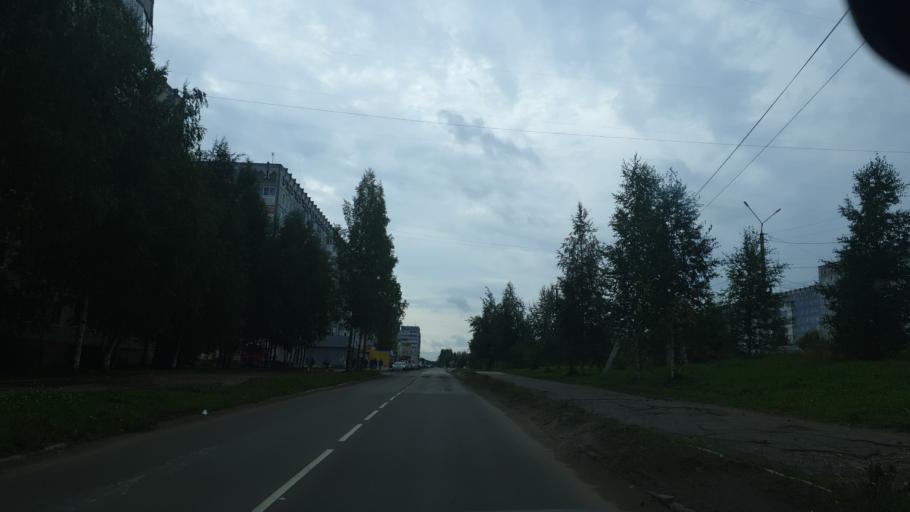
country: RU
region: Komi Republic
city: Ezhva
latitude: 61.7867
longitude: 50.7450
